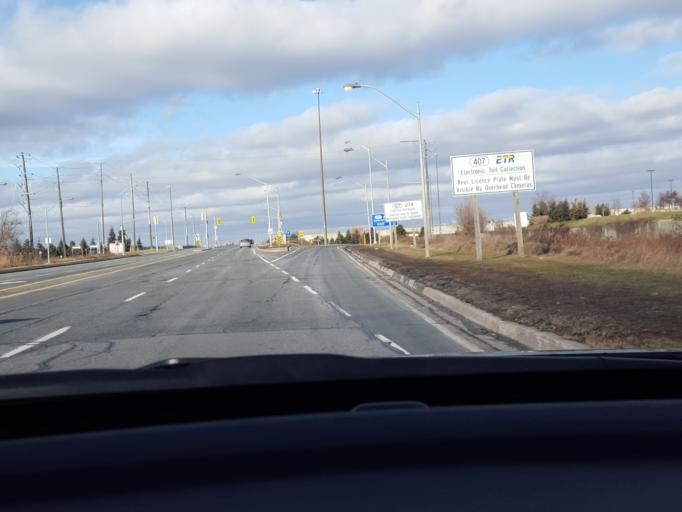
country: CA
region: Ontario
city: Concord
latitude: 43.7708
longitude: -79.5695
